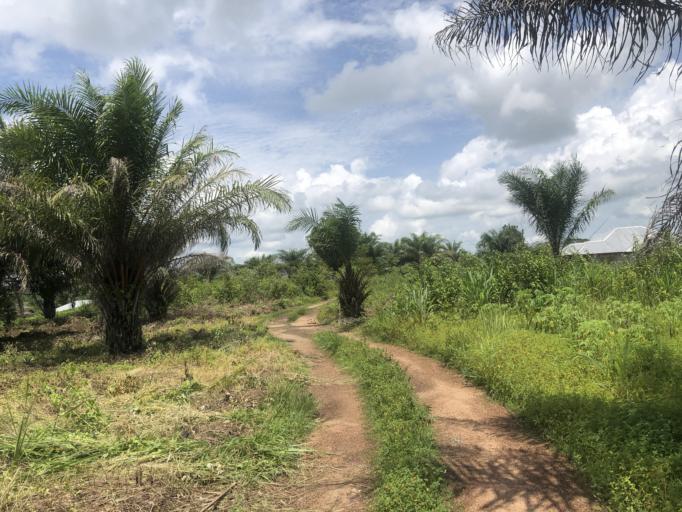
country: SL
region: Northern Province
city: Magburaka
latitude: 8.7100
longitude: -11.9408
